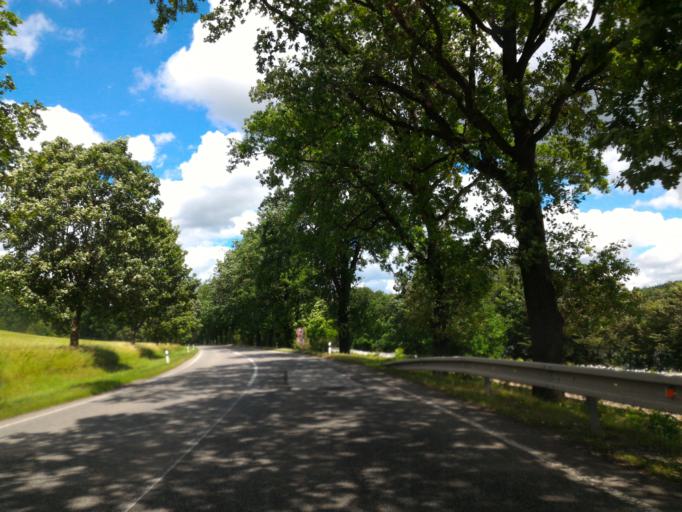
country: CZ
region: Vysocina
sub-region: Okres Jihlava
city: Trest'
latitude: 49.3135
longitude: 15.4811
